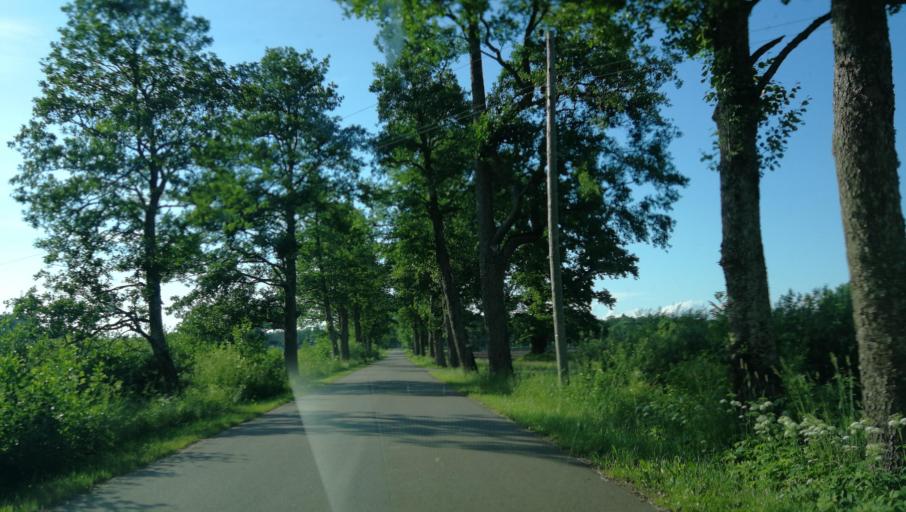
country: LV
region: Pargaujas
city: Stalbe
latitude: 57.3544
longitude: 25.0926
